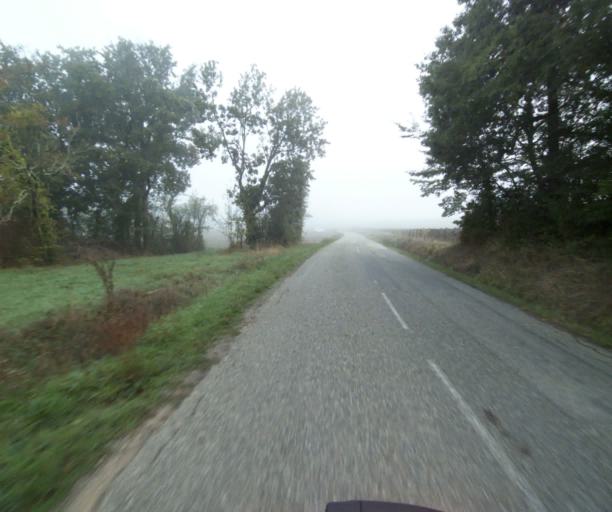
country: FR
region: Midi-Pyrenees
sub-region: Departement du Tarn-et-Garonne
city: Orgueil
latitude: 43.9344
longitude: 1.4192
